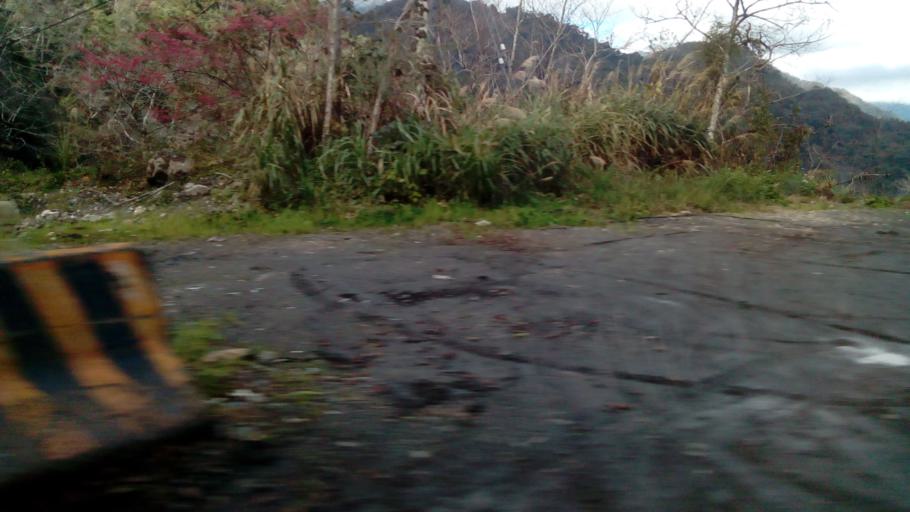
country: TW
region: Taiwan
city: Daxi
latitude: 24.4036
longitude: 121.3615
